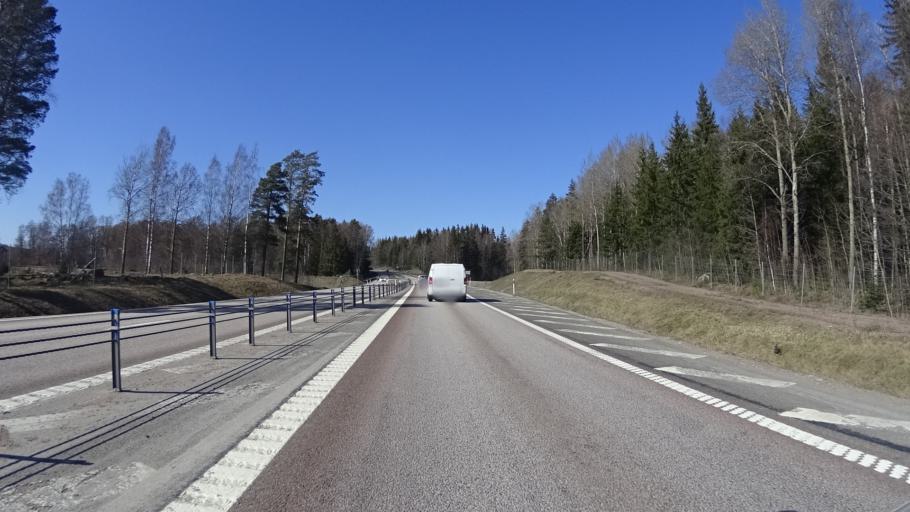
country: SE
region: Vaermland
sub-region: Kristinehamns Kommun
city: Kristinehamn
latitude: 59.3488
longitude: 14.0813
